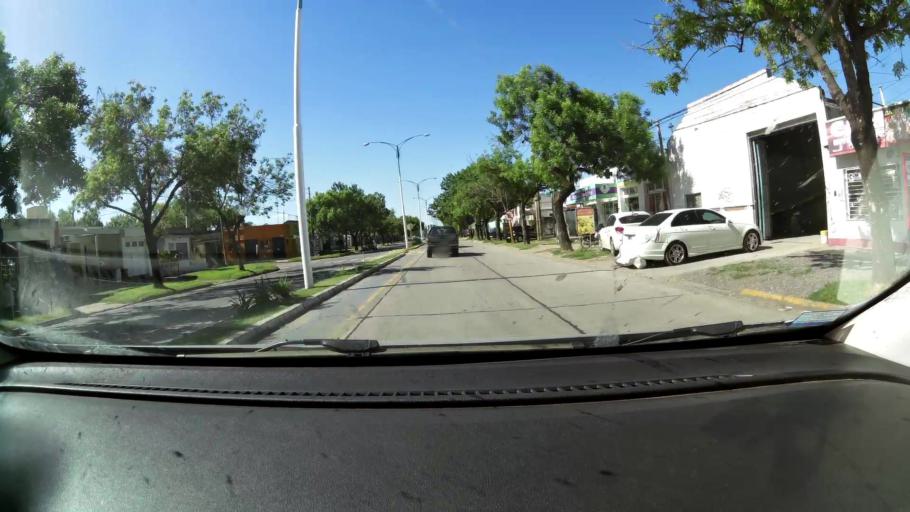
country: AR
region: Santa Fe
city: Rafaela
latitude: -31.2405
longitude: -61.4889
